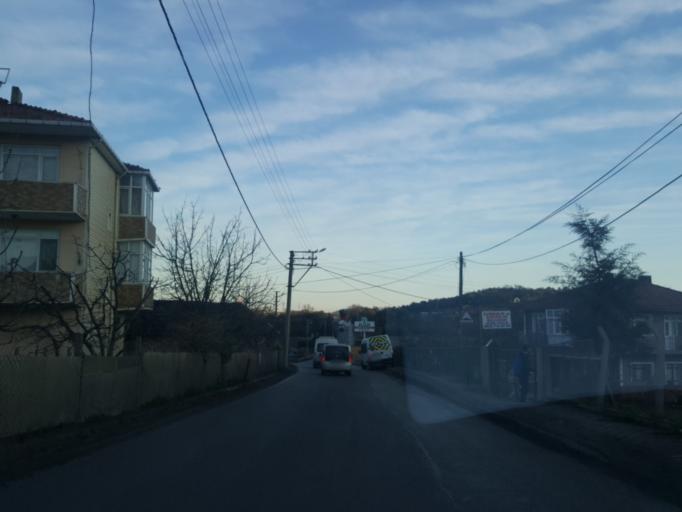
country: TR
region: Kocaeli
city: Tavsanli
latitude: 40.8484
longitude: 29.5550
